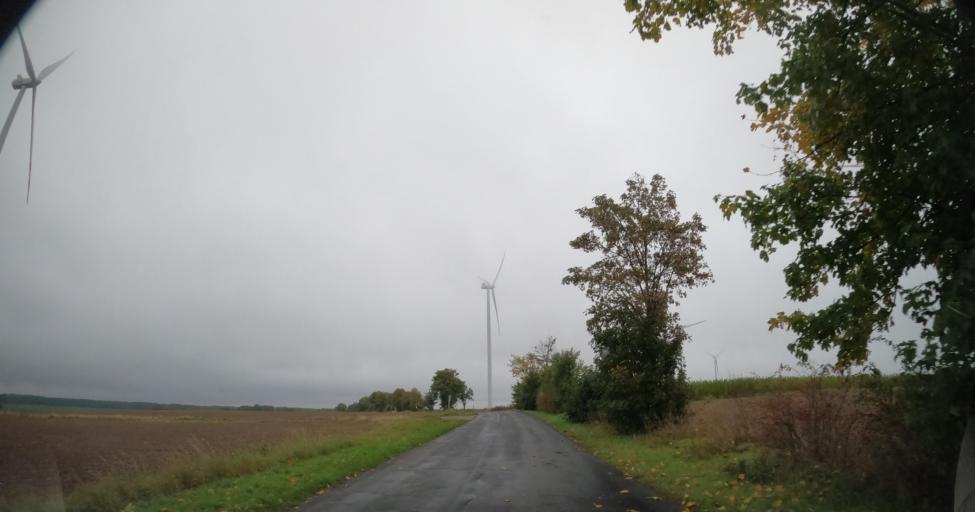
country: PL
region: West Pomeranian Voivodeship
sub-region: Powiat pyrzycki
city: Kozielice
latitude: 53.0805
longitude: 14.7788
